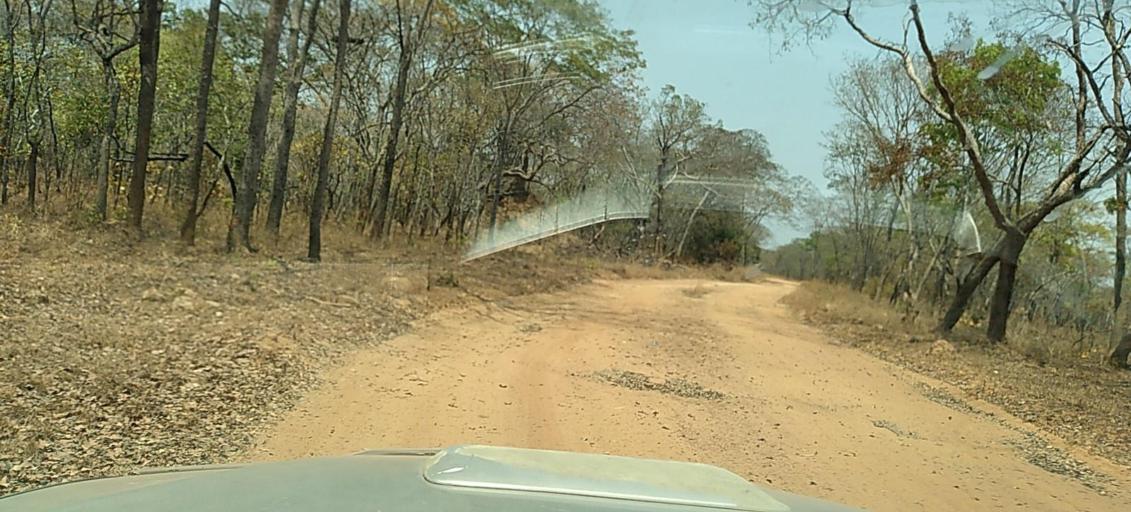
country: ZM
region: North-Western
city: Kasempa
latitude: -13.6102
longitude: 26.1954
